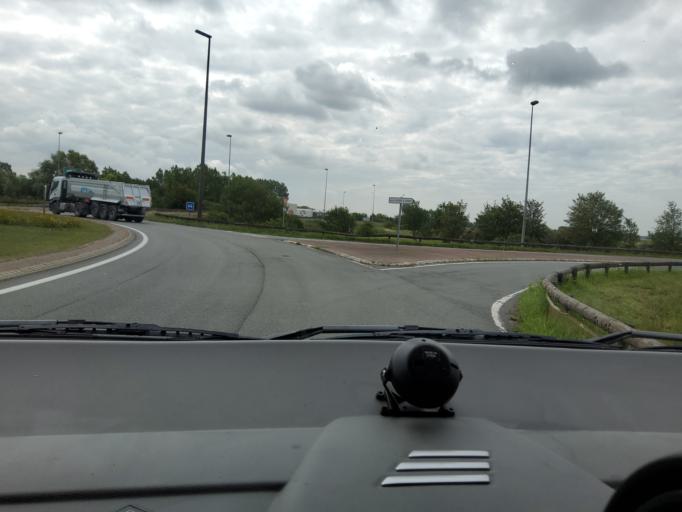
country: FR
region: Nord-Pas-de-Calais
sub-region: Departement du Nord
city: Loon-Plage
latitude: 50.9951
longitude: 2.2005
